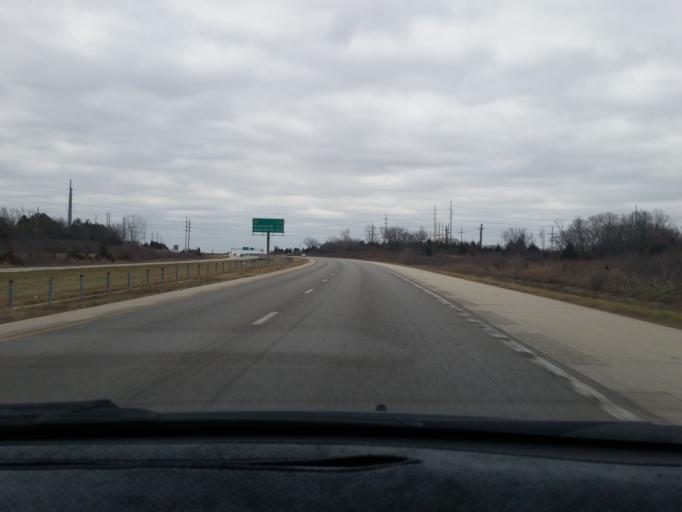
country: US
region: Kansas
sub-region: Johnson County
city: Olathe
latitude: 38.9417
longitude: -94.8667
